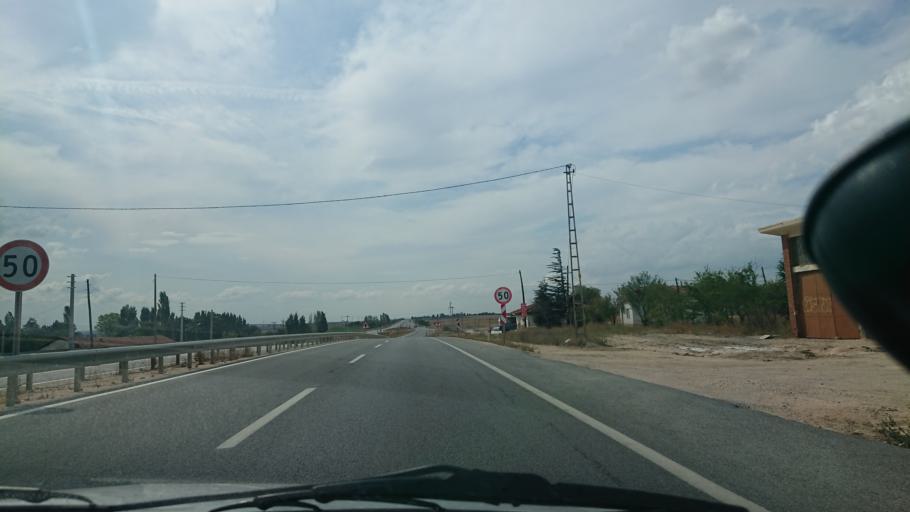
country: TR
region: Eskisehir
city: Inonu
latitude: 39.7260
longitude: 30.2971
